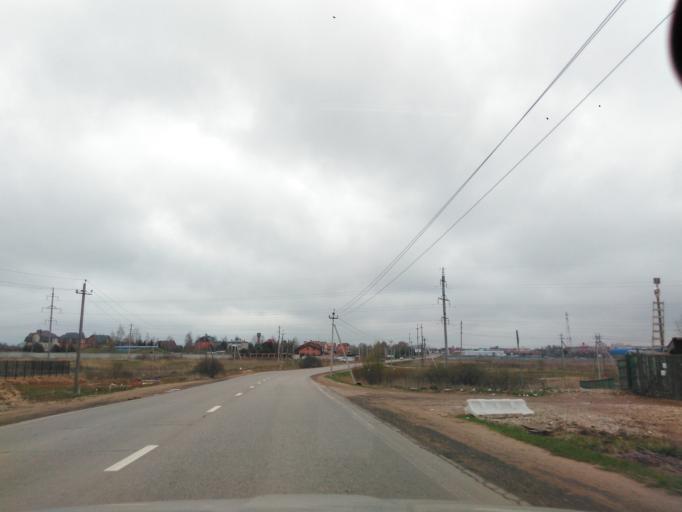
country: RU
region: Moskovskaya
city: Pavlovskaya Sloboda
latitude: 55.8197
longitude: 37.0621
